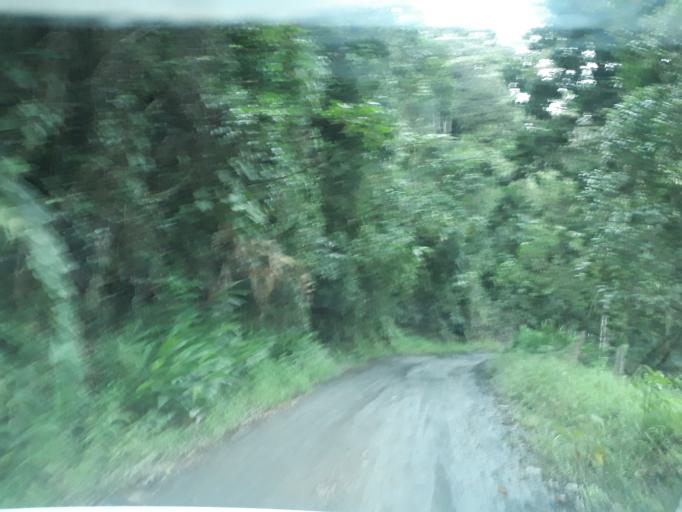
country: CO
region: Boyaca
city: Muzo
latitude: 5.3705
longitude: -74.0719
